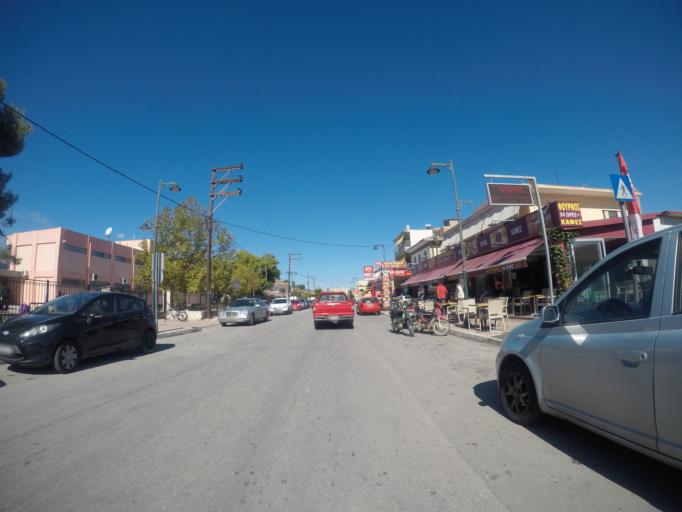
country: GR
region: West Greece
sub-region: Nomos Aitolias kai Akarnanias
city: Vonitsa
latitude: 38.9151
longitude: 20.8898
